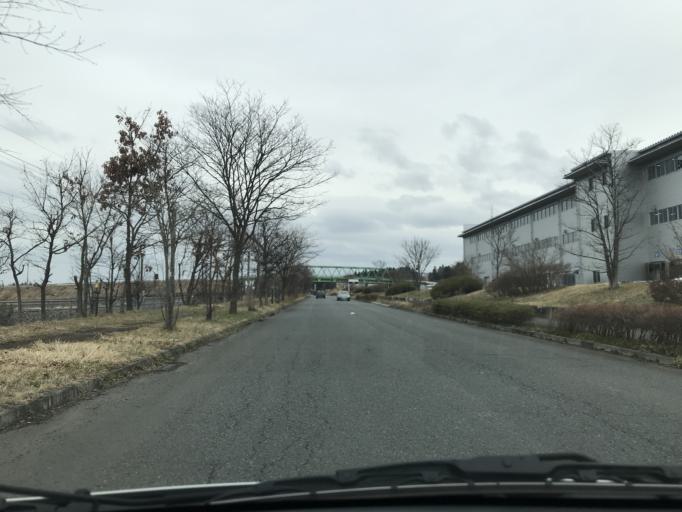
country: JP
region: Iwate
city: Kitakami
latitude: 39.2519
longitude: 141.1038
